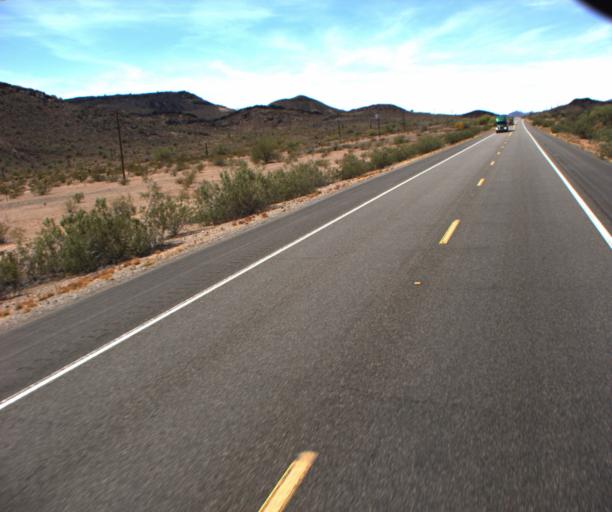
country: US
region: Arizona
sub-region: La Paz County
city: Quartzsite
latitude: 33.6866
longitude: -113.9174
